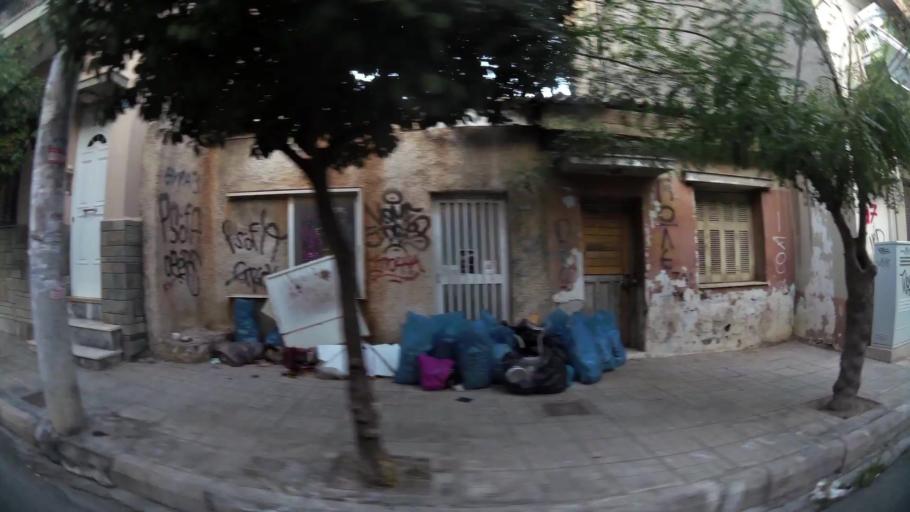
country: GR
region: Attica
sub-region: Nomos Piraios
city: Nikaia
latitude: 37.9729
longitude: 23.6444
